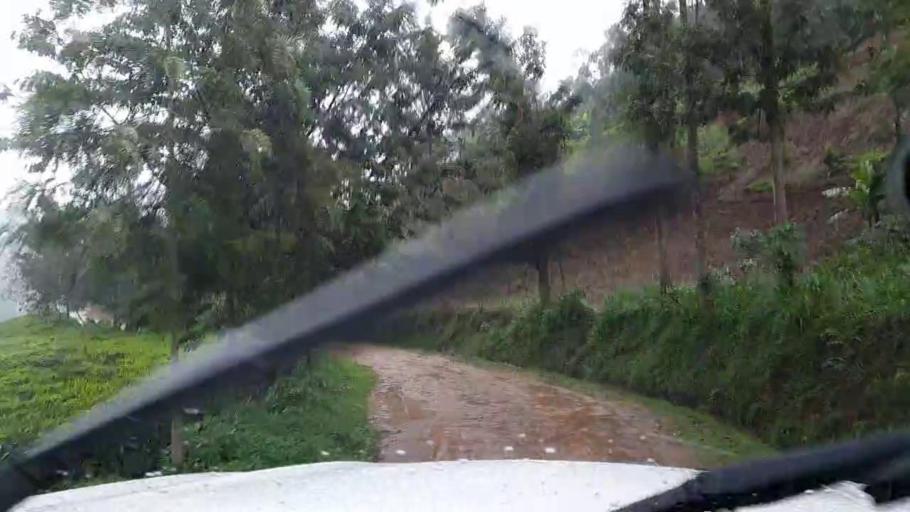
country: RW
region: Northern Province
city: Byumba
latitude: -1.6516
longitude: 29.9173
